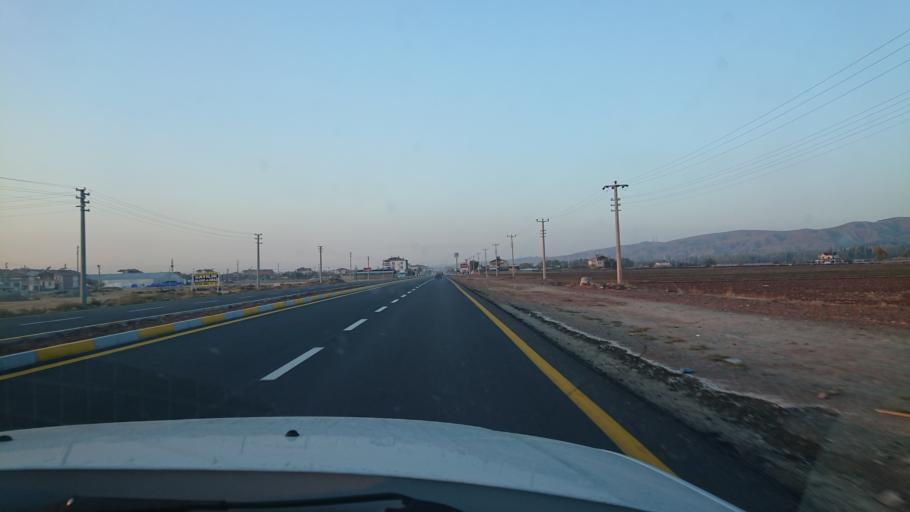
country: TR
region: Aksaray
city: Aksaray
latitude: 38.3276
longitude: 34.0517
